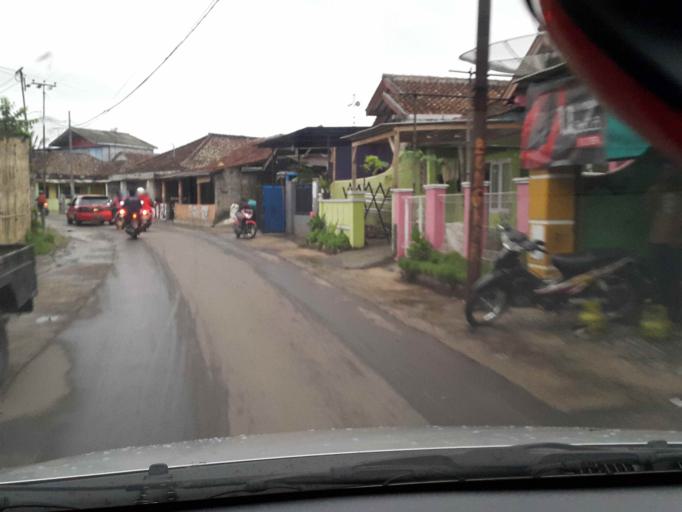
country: ID
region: West Java
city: Sukabumi
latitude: -6.9129
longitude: 106.8763
